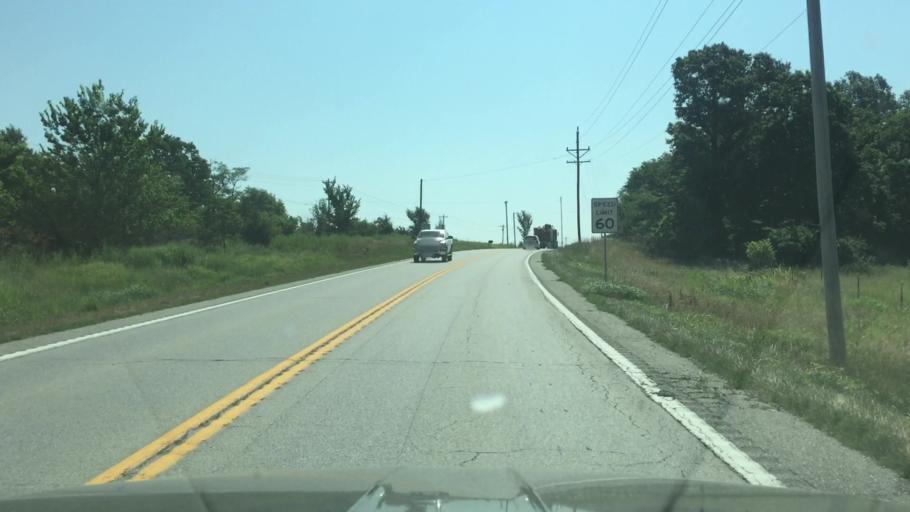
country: US
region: Missouri
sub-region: Moniteau County
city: Tipton
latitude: 38.6719
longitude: -92.8553
